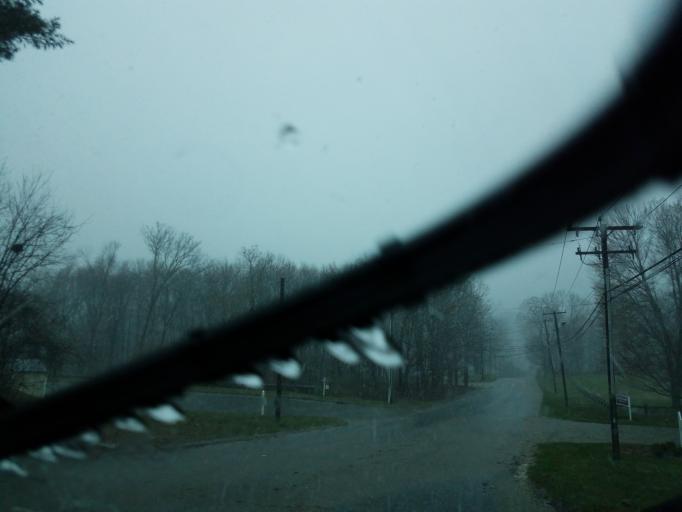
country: US
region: Connecticut
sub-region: New Haven County
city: Waterbury
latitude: 41.5329
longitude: -73.0811
